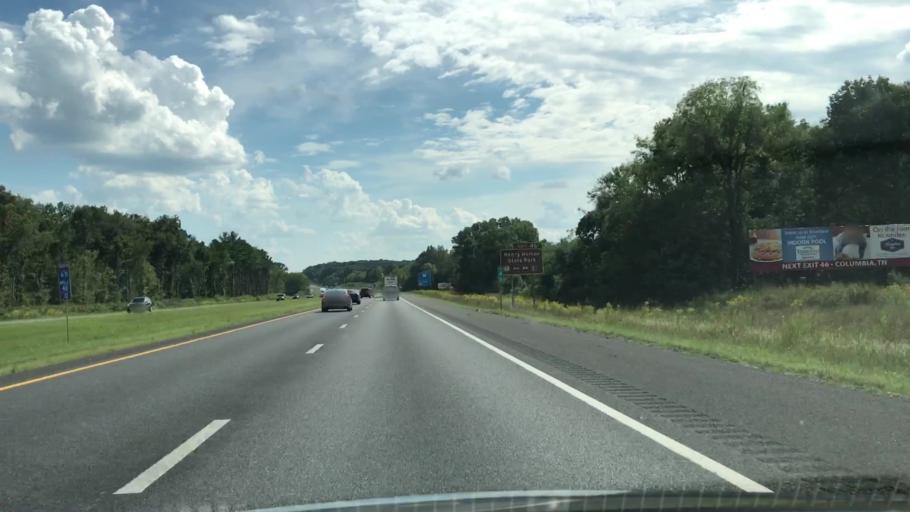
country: US
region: Tennessee
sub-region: Maury County
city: Spring Hill
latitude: 35.6714
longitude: -86.8909
